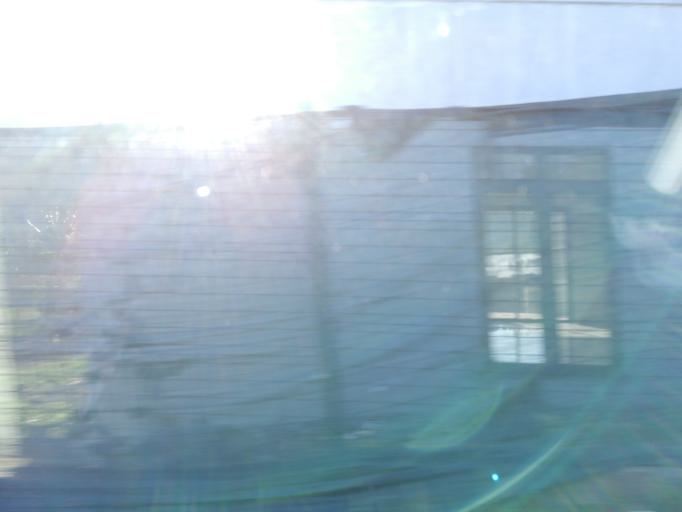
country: MU
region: Moka
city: Saint Pierre
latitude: -20.2119
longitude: 57.5241
